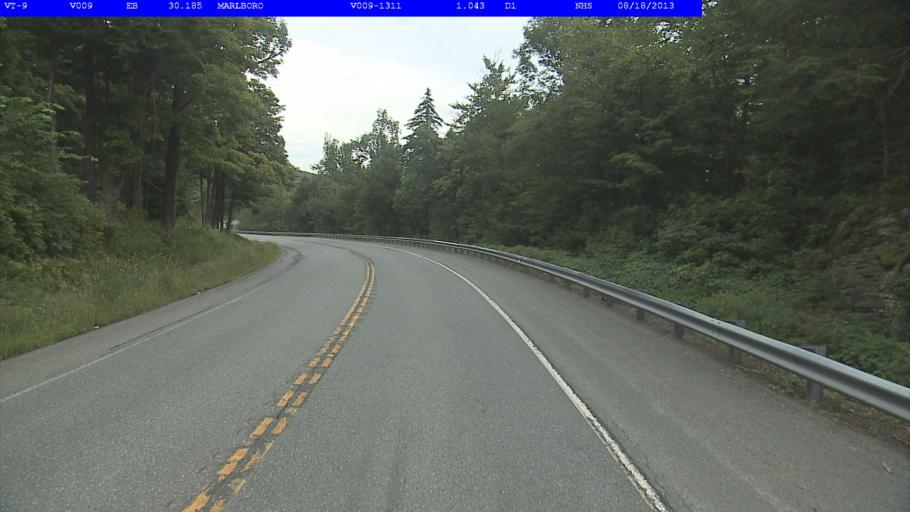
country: US
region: Vermont
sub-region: Windham County
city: Dover
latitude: 42.8567
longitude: -72.7890
